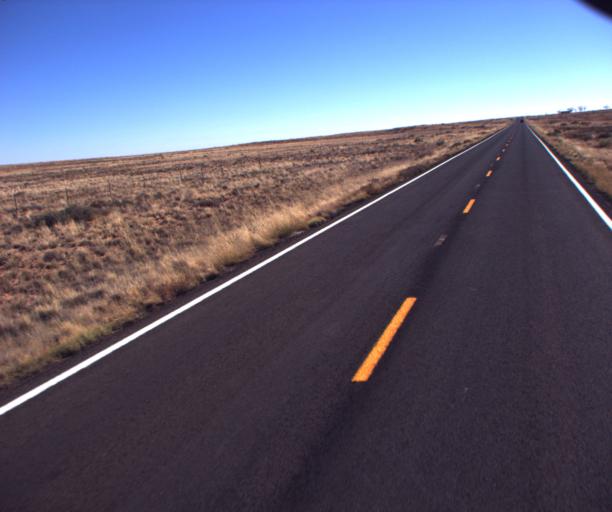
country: US
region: Arizona
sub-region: Coconino County
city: Tuba City
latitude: 35.9639
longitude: -110.9468
